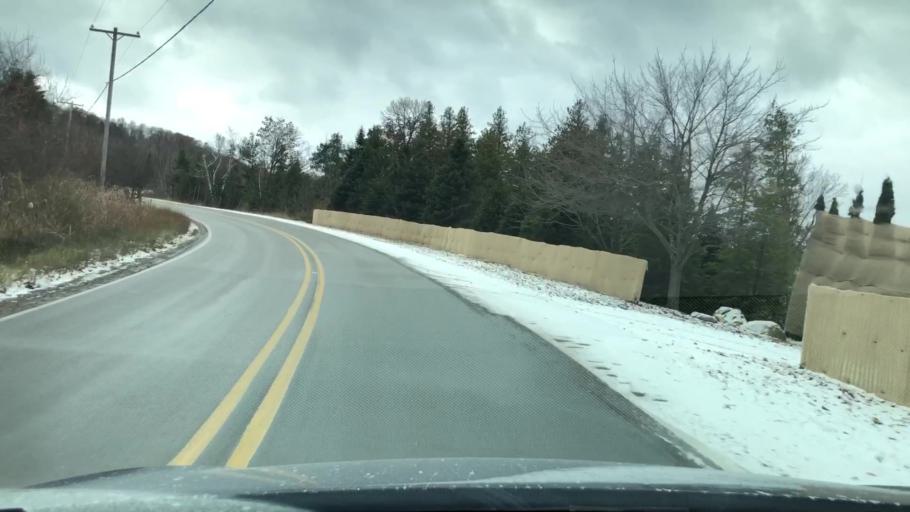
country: US
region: Michigan
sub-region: Leelanau County
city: Greilickville
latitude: 44.8380
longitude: -85.5617
